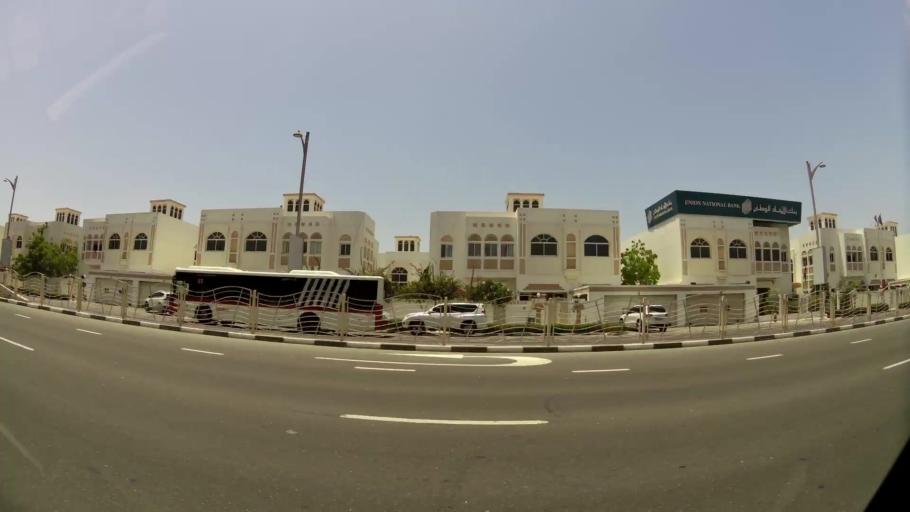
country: AE
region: Dubai
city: Dubai
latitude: 25.2226
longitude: 55.2567
